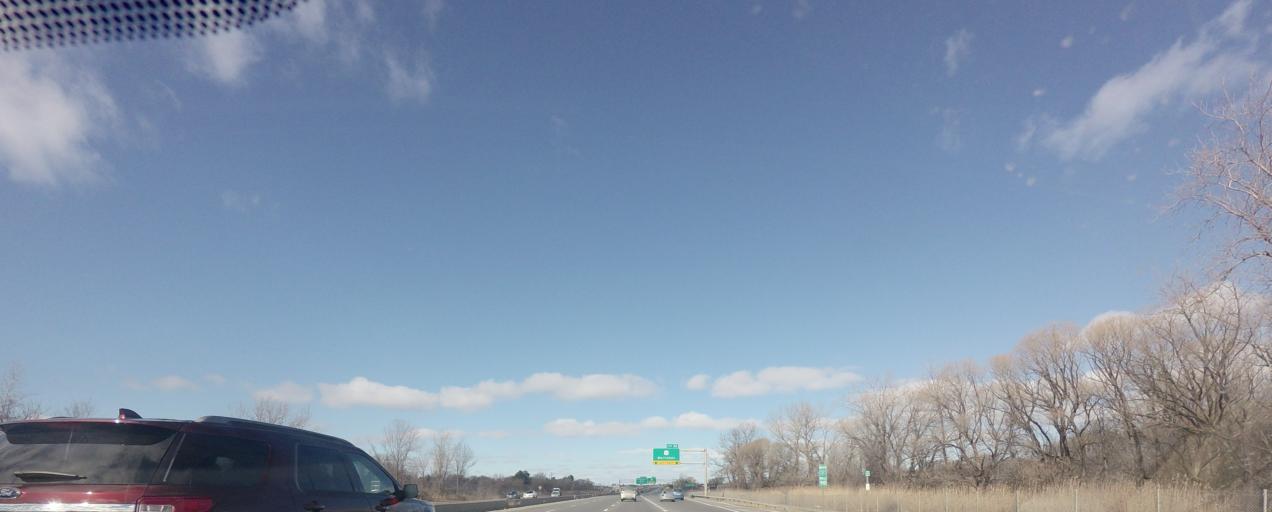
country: US
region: New York
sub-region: Onondaga County
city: Mattydale
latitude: 43.1045
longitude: -76.1527
